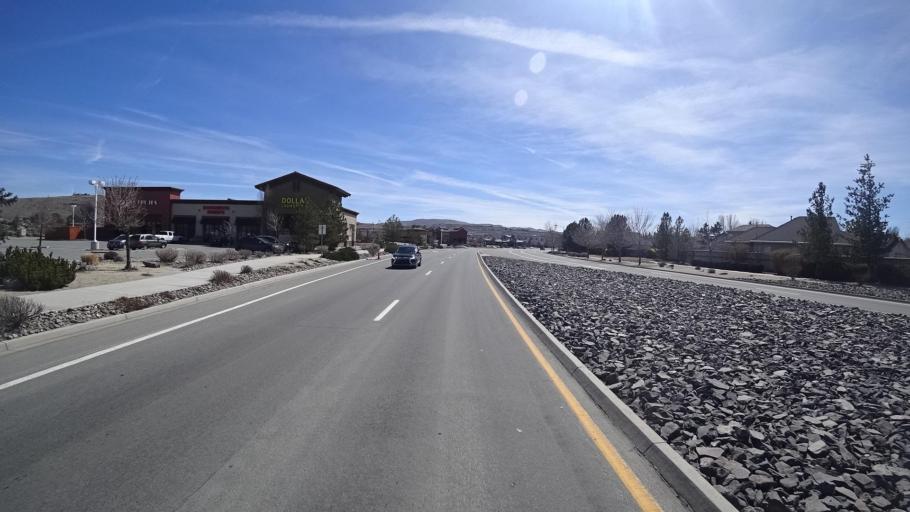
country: US
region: Nevada
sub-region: Washoe County
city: Sun Valley
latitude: 39.5883
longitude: -119.7266
